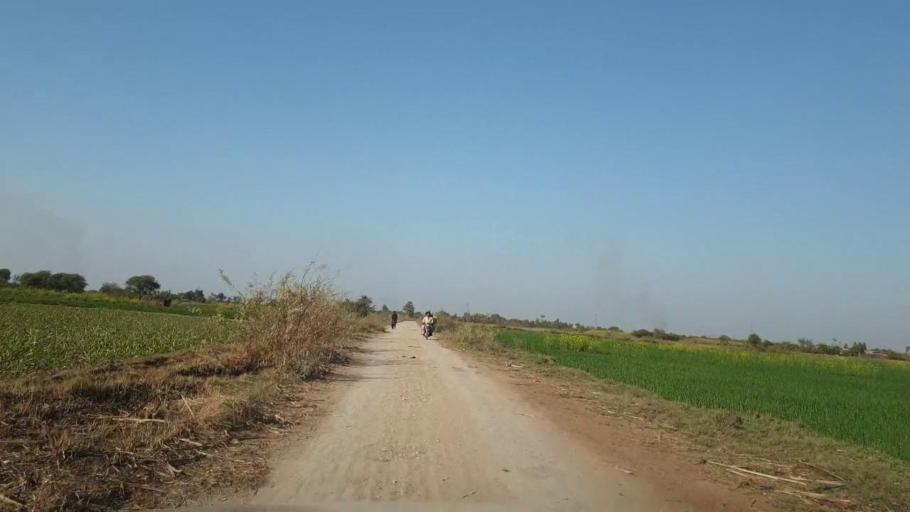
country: PK
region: Sindh
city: Tando Allahyar
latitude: 25.5043
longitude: 68.6540
